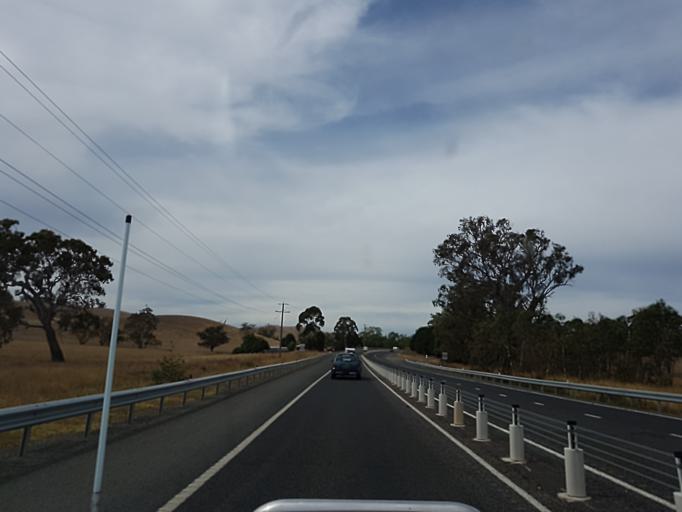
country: AU
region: Victoria
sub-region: Murrindindi
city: Alexandra
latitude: -37.2026
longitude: 145.4645
